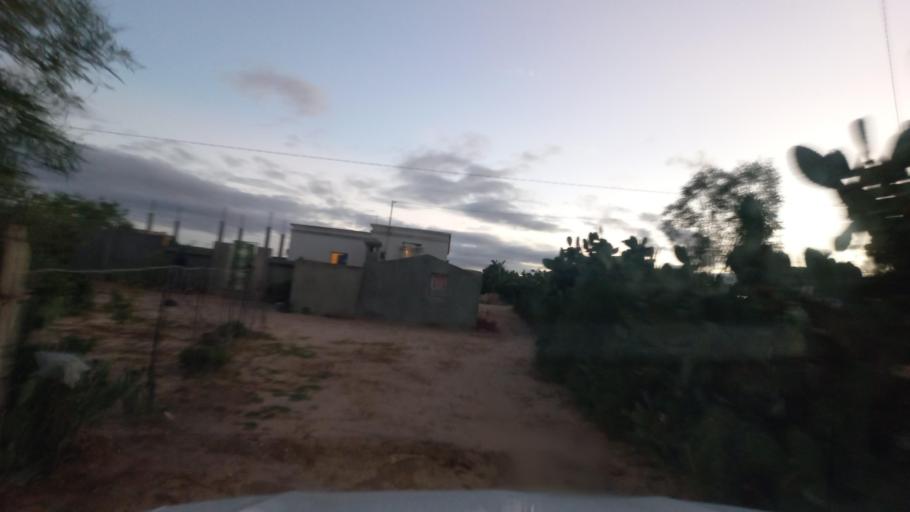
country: TN
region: Al Qasrayn
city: Kasserine
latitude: 35.2580
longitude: 8.9385
